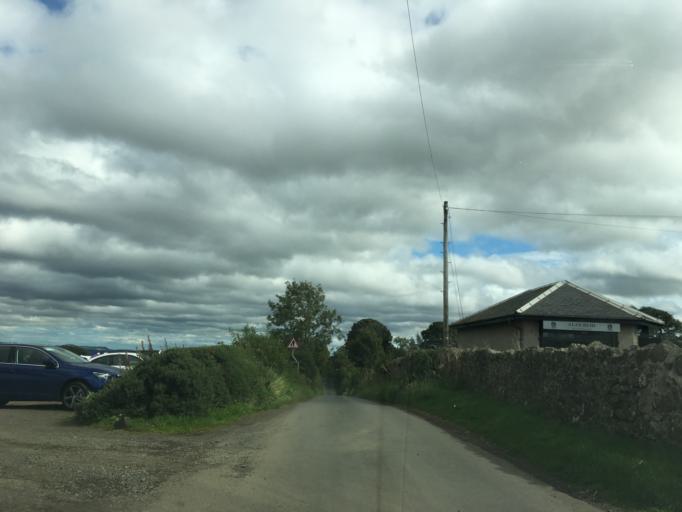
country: GB
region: Scotland
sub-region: West Lothian
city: Linlithgow
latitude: 55.9970
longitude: -3.5979
